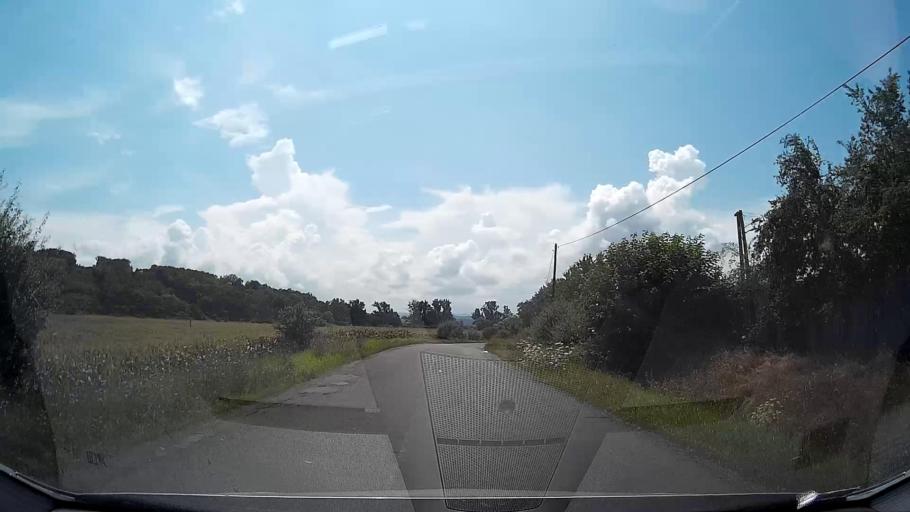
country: SK
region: Banskobystricky
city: Fil'akovo
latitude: 48.3216
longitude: 19.8140
